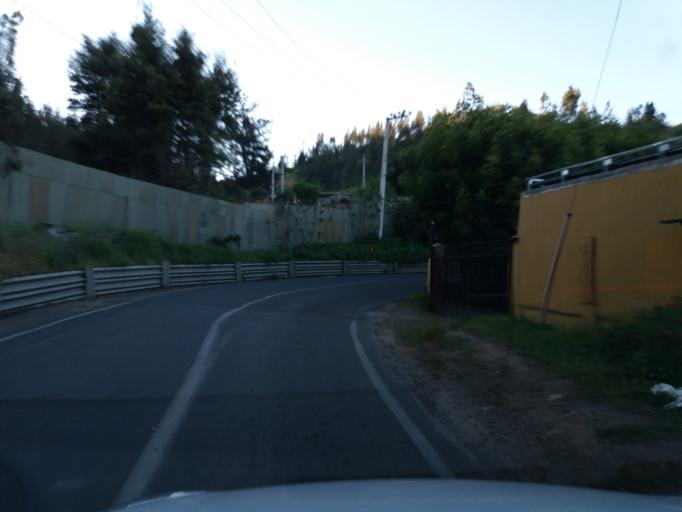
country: CL
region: Valparaiso
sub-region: Provincia de Quillota
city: Quillota
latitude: -32.8778
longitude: -71.2739
